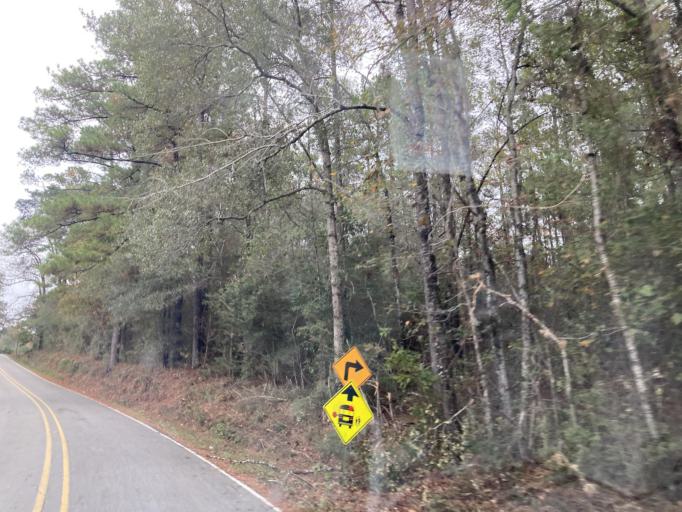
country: US
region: Mississippi
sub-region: Lamar County
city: Purvis
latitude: 31.1885
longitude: -89.4233
